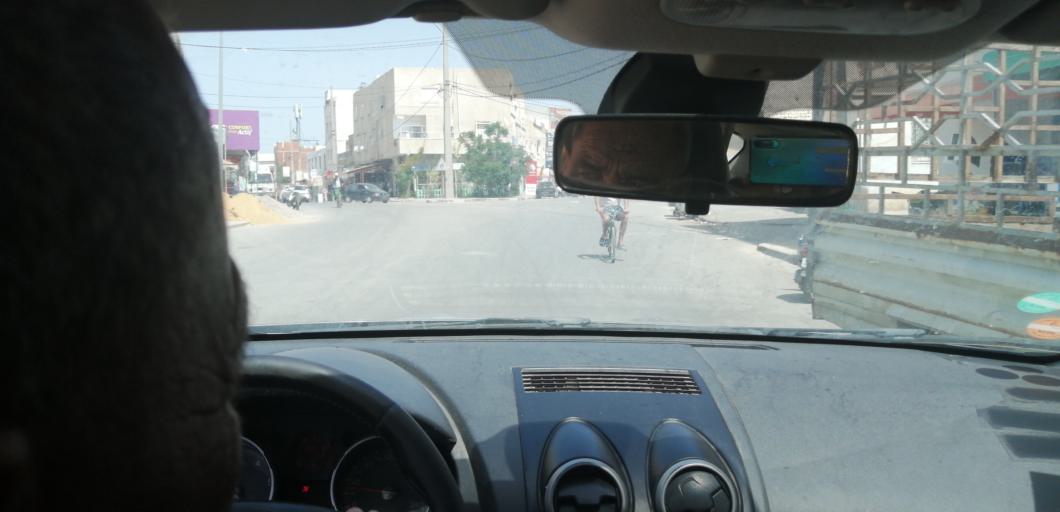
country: TN
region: Al Qayrawan
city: Kairouan
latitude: 35.6781
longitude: 10.0900
